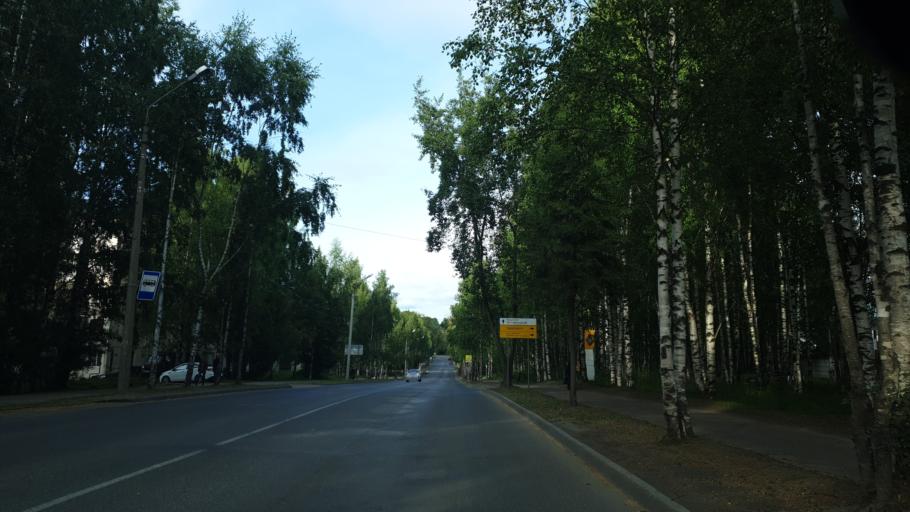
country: RU
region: Komi Republic
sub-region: Syktyvdinskiy Rayon
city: Syktyvkar
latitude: 61.6583
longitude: 50.8114
